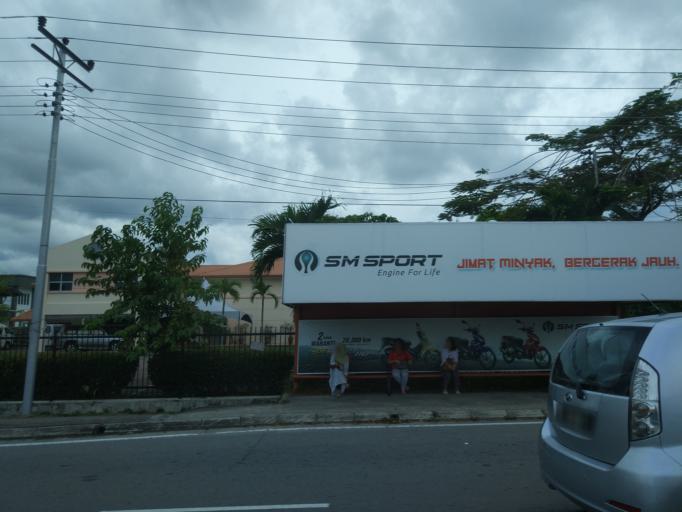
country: MY
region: Sabah
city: Kota Kinabalu
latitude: 5.9767
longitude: 116.0949
